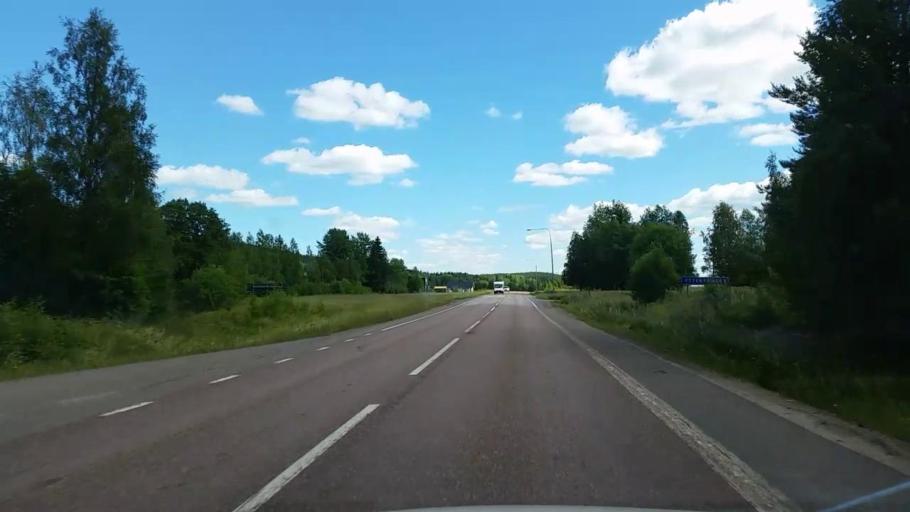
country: SE
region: Dalarna
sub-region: Faluns Kommun
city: Svardsjo
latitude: 60.8490
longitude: 15.7550
